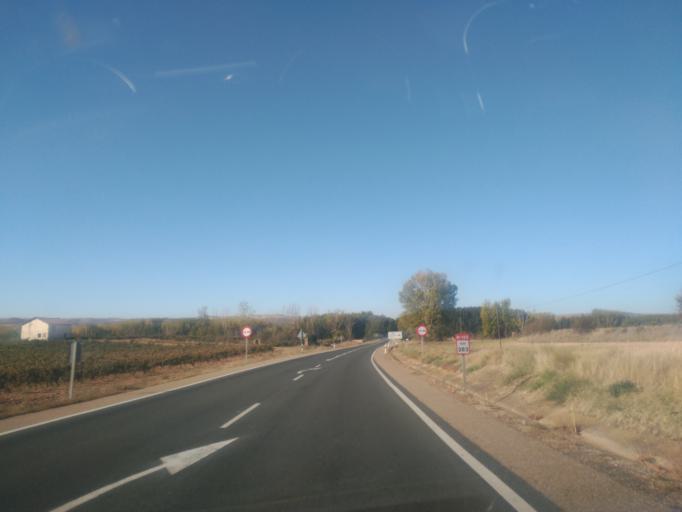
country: ES
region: Castille and Leon
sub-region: Provincia de Burgos
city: Haza
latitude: 41.6330
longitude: -3.8376
